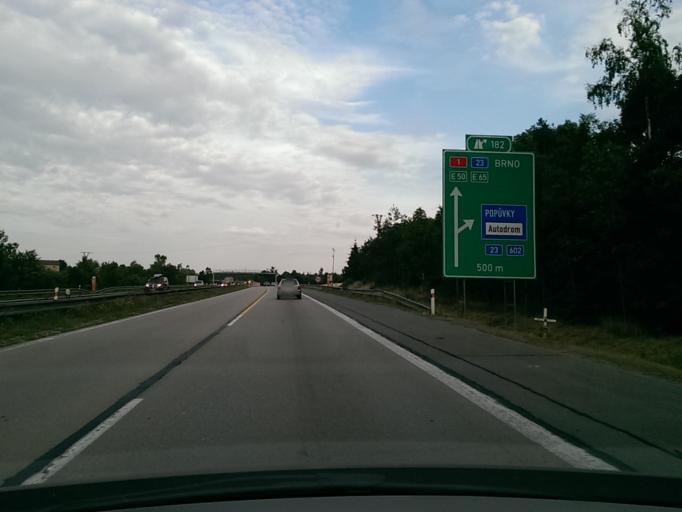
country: CZ
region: South Moravian
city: Ricany
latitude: 49.1925
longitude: 16.4357
